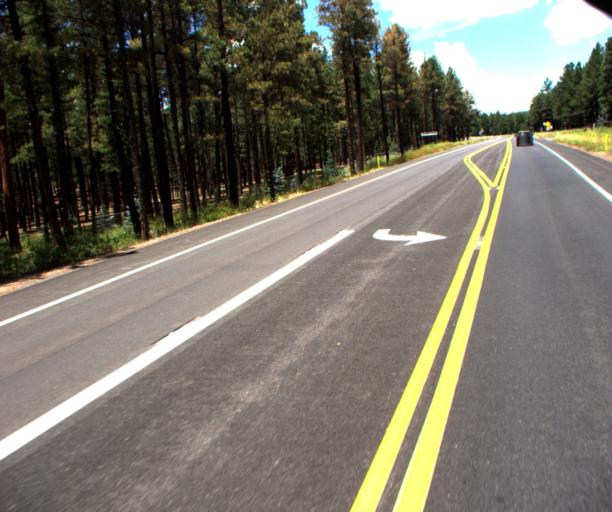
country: US
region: Arizona
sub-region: Coconino County
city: Flagstaff
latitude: 35.2439
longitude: -111.6854
